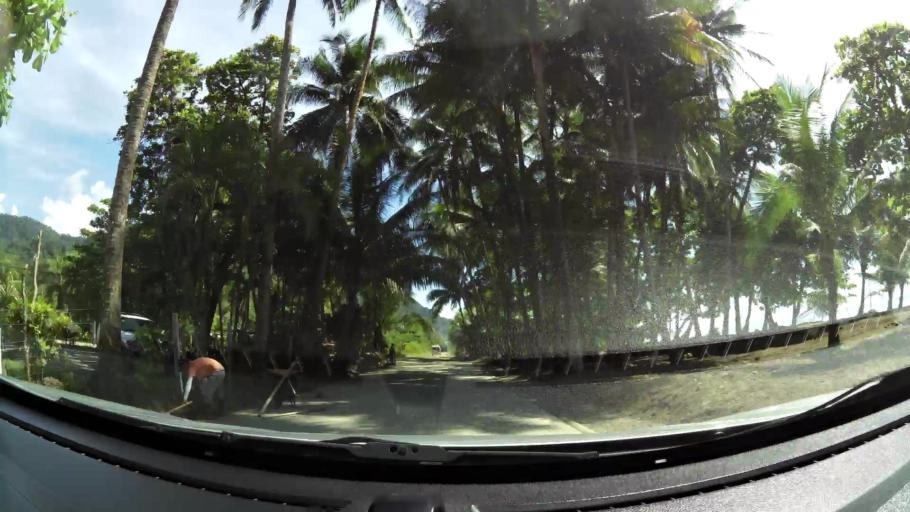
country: CR
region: San Jose
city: San Isidro
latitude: 9.2519
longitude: -83.8644
